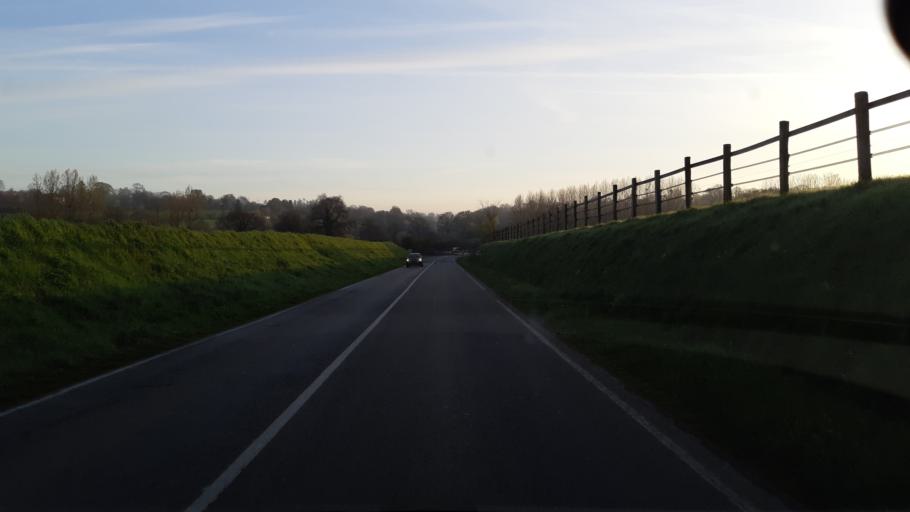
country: FR
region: Lower Normandy
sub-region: Departement de la Manche
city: Agneaux
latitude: 49.0667
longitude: -1.1317
